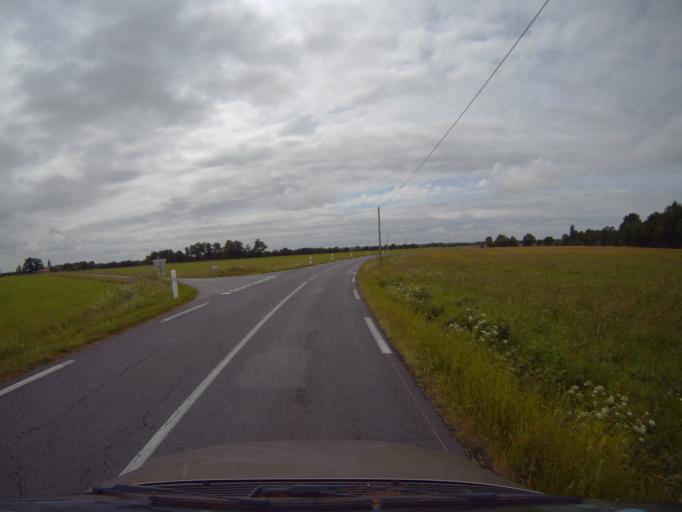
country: FR
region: Pays de la Loire
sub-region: Departement de la Loire-Atlantique
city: Aigrefeuille-sur-Maine
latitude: 47.0601
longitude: -1.4432
